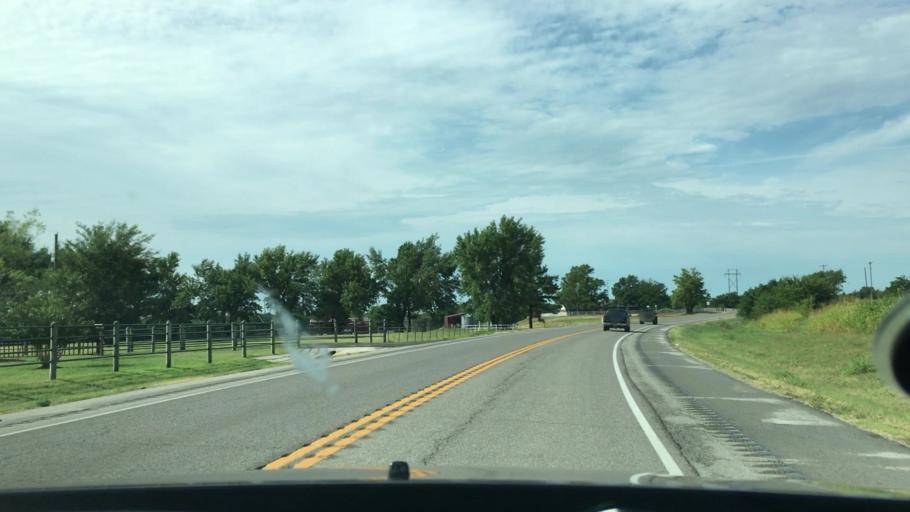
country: US
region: Oklahoma
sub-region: Murray County
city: Sulphur
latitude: 34.5312
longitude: -96.9676
